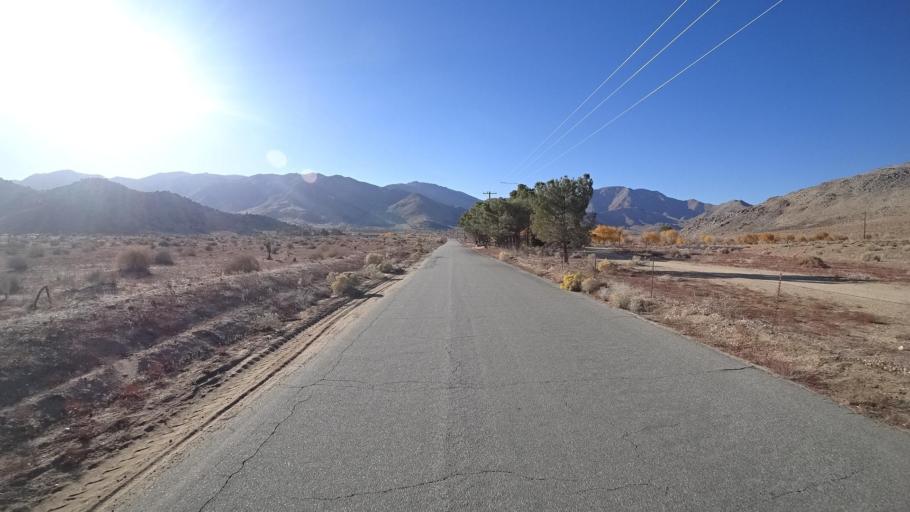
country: US
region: California
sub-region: Kern County
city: Weldon
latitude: 35.5577
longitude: -118.2295
